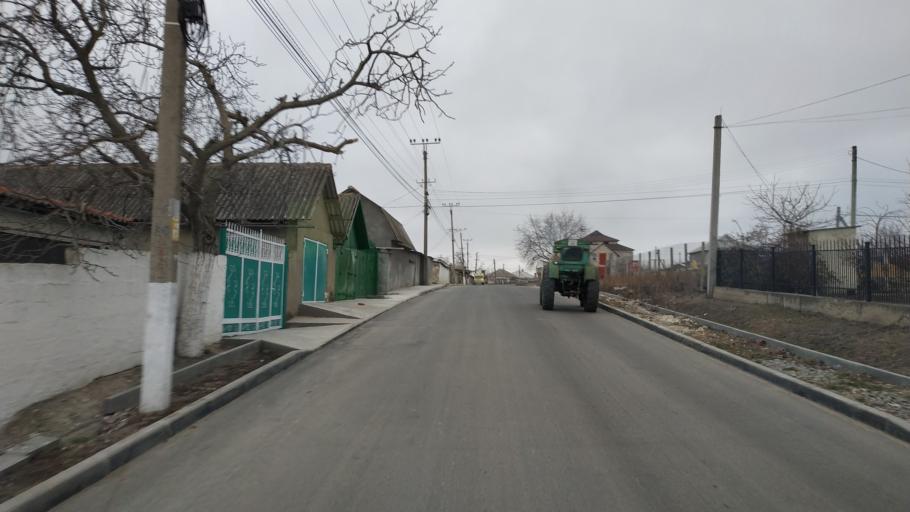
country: MD
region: Laloveni
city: Ialoveni
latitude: 46.9064
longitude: 28.7992
